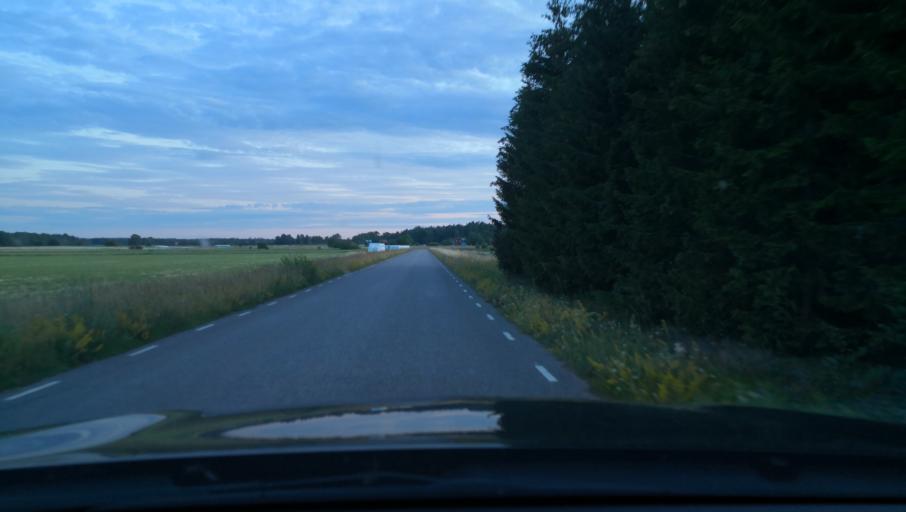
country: SE
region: Uppsala
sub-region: Osthammars Kommun
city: Bjorklinge
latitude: 60.0484
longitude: 17.5079
